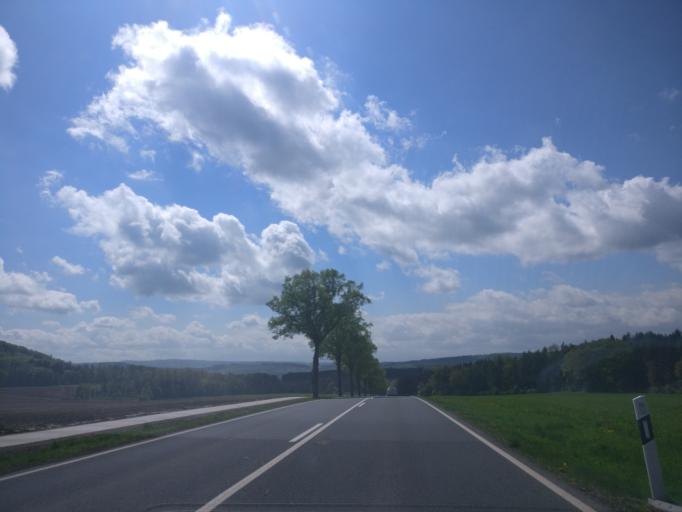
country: DE
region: Lower Saxony
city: Dransfeld
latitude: 51.4893
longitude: 9.7280
